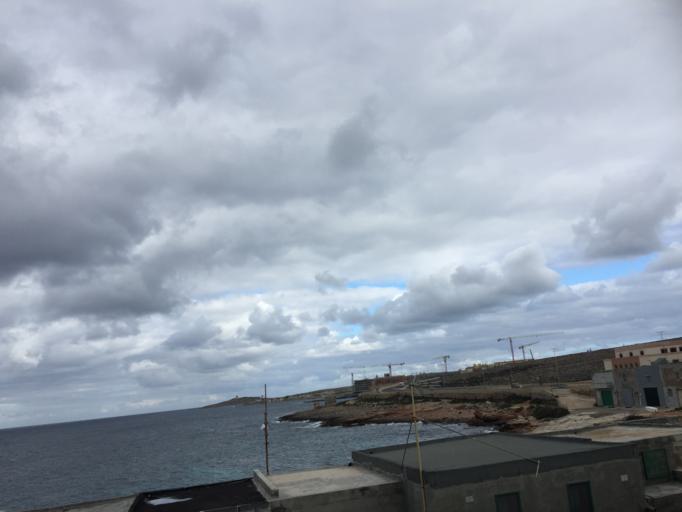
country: MT
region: Il-Mellieha
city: Mellieha
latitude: 35.9862
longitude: 14.3372
